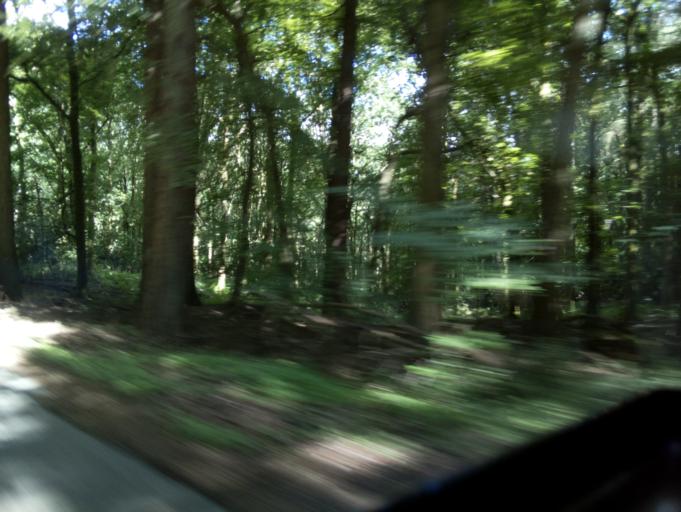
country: GB
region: England
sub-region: Gloucestershire
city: Cinderford
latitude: 51.7866
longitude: -2.4993
